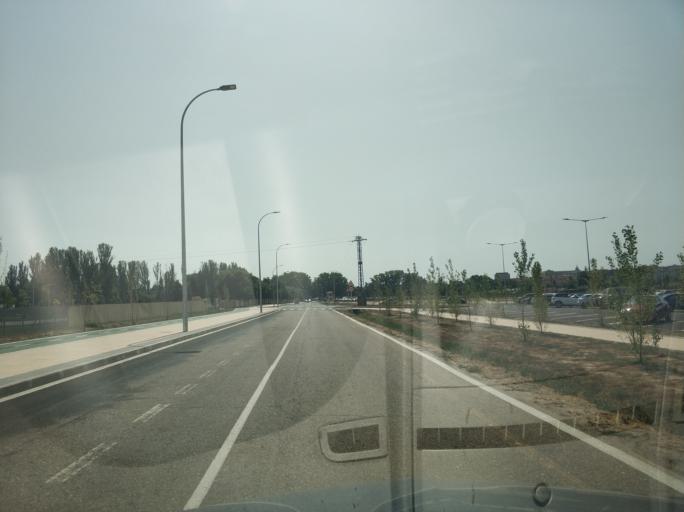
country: ES
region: Castille and Leon
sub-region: Provincia de Salamanca
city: Santa Marta de Tormes
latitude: 40.9624
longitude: -5.6362
